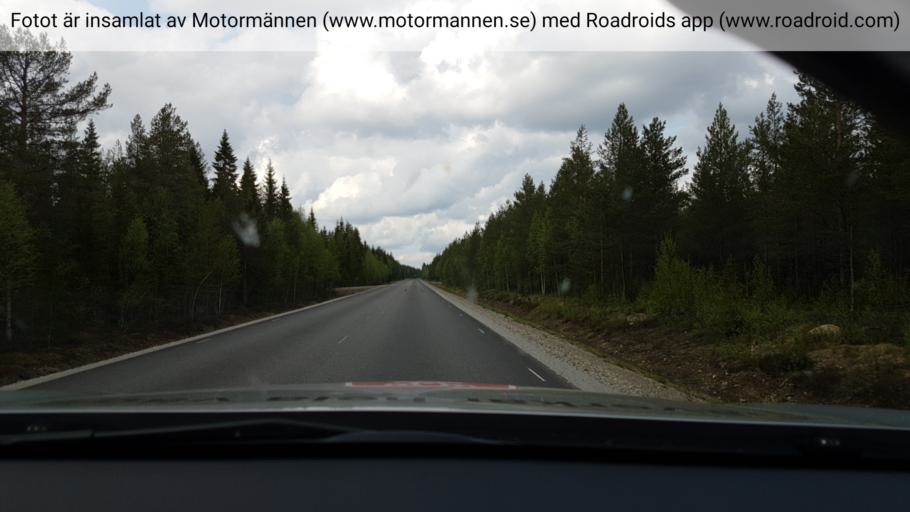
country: SE
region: Vaesterbotten
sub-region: Lycksele Kommun
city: Lycksele
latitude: 64.0466
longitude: 18.4323
